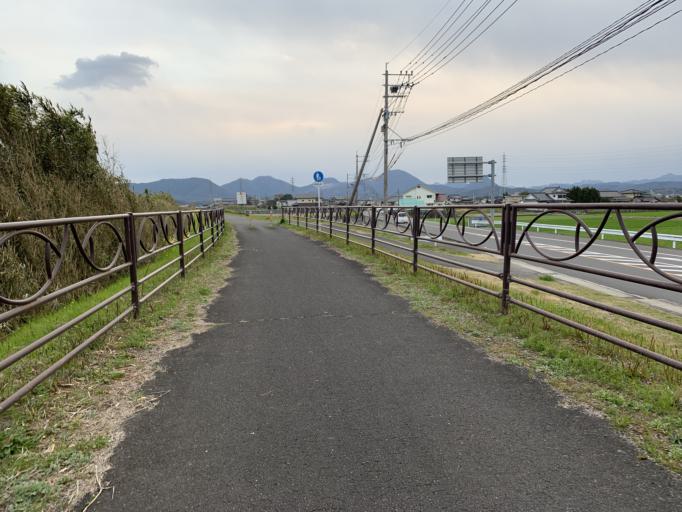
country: JP
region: Oita
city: Bungo-Takada-shi
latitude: 33.5411
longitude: 131.3541
